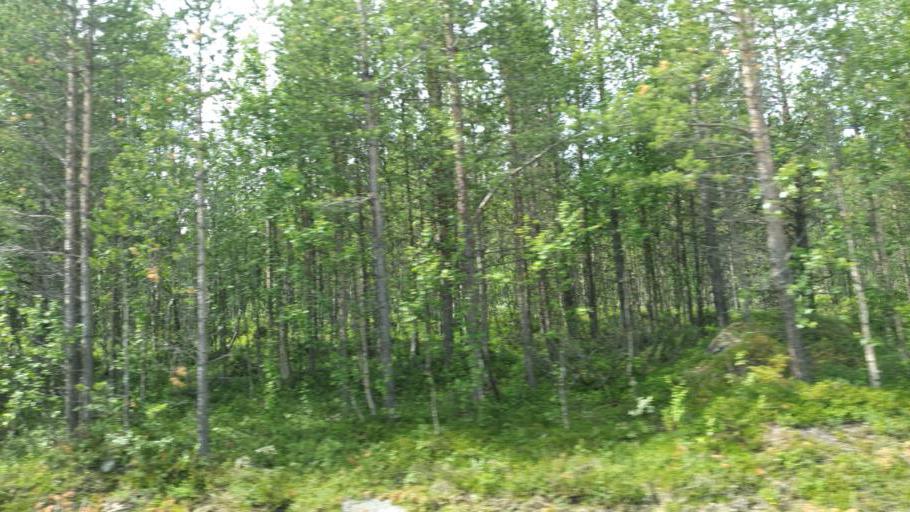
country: NO
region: Oppland
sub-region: Vaga
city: Vagamo
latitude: 61.6862
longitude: 9.0585
